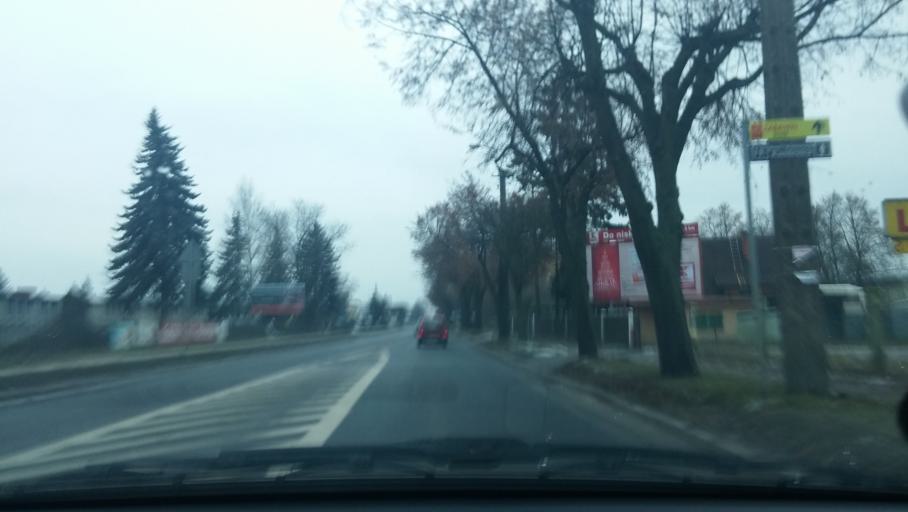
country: PL
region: Masovian Voivodeship
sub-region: Siedlce
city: Siedlce
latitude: 52.1946
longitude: 22.2645
